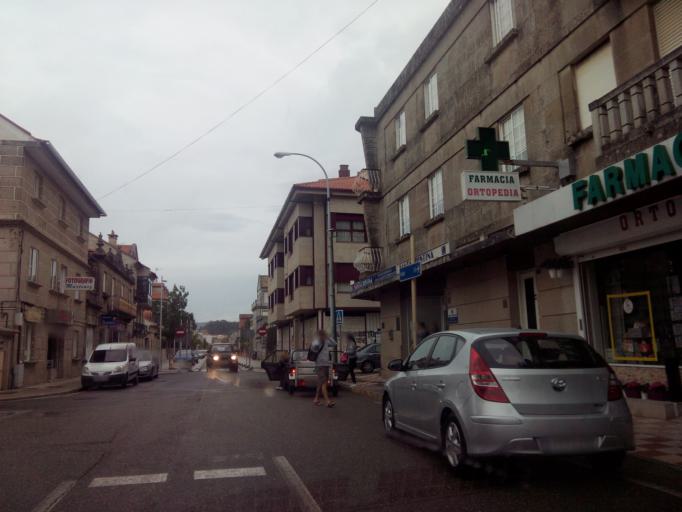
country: ES
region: Galicia
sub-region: Provincia de Pontevedra
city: Baiona
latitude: 42.1111
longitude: -8.8193
